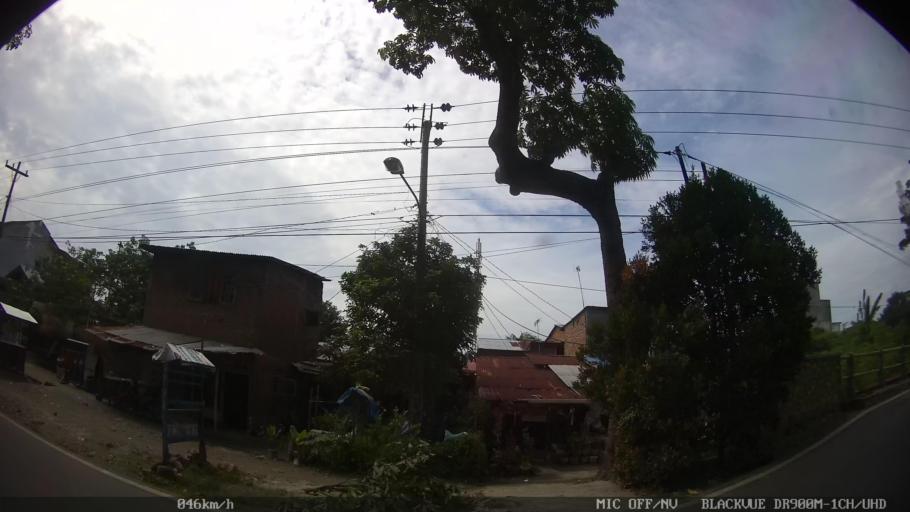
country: ID
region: North Sumatra
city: Medan
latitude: 3.6225
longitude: 98.6935
